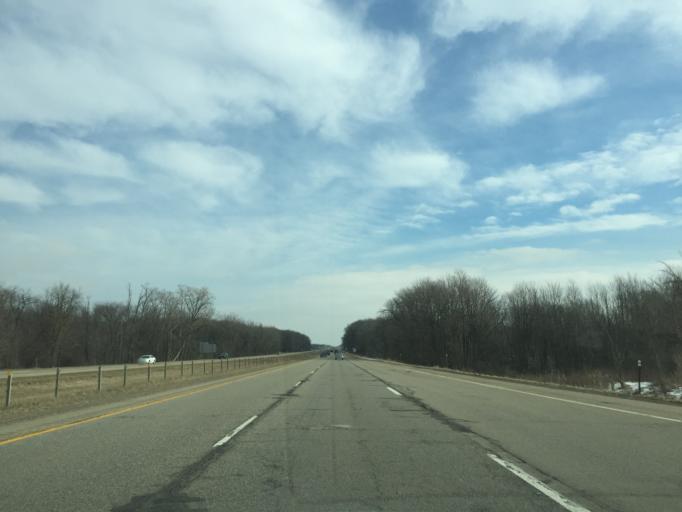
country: US
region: Michigan
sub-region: Ionia County
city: Ionia
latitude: 42.8790
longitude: -85.0688
